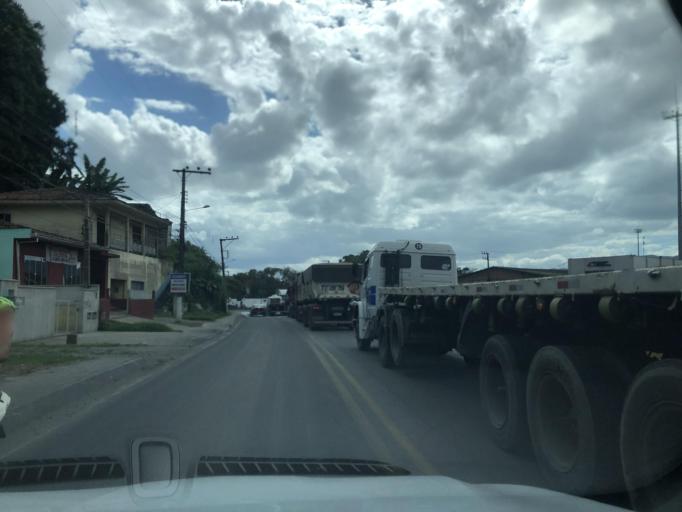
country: BR
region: Santa Catarina
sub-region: Sao Francisco Do Sul
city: Sao Francisco do Sul
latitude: -26.2410
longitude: -48.6336
